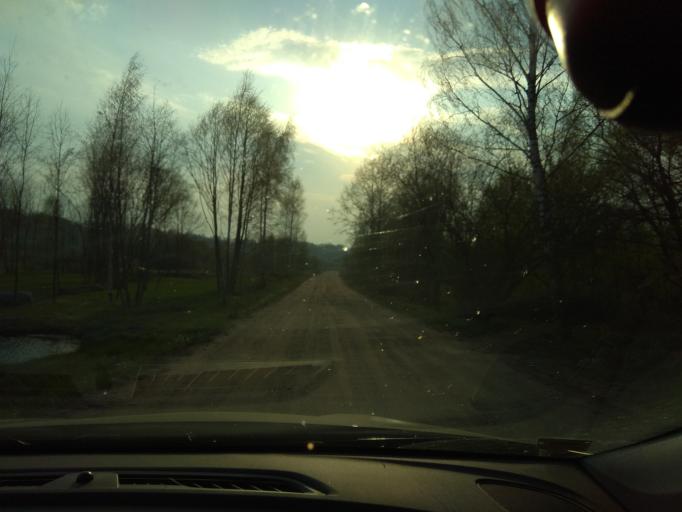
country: LT
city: Baltoji Voke
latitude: 54.5953
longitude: 25.1850
